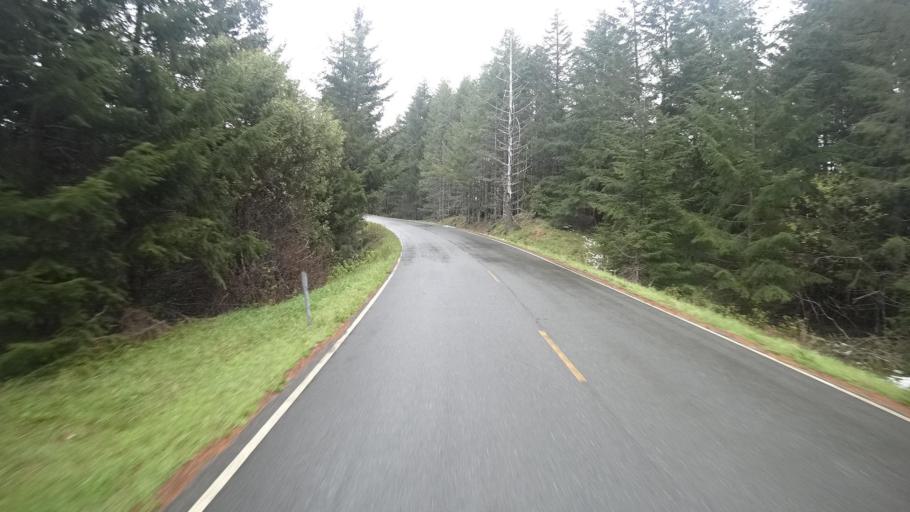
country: US
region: California
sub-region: Humboldt County
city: Westhaven-Moonstone
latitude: 41.1428
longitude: -123.8534
